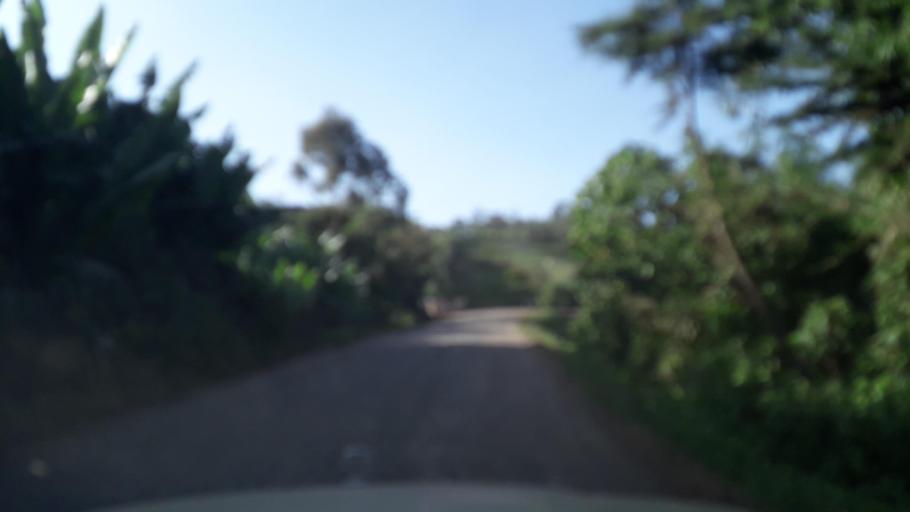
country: ET
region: Oromiya
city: Jima
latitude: 7.4410
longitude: 36.8791
